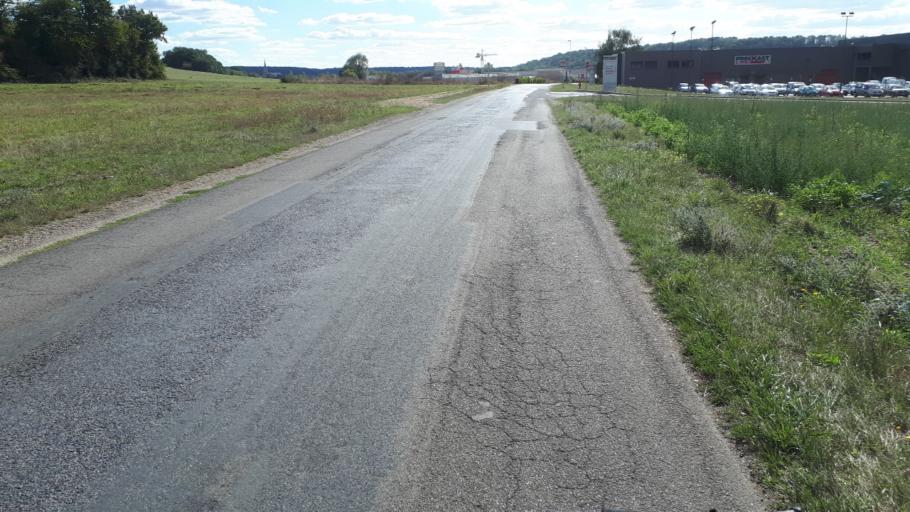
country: FR
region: Centre
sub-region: Departement du Loir-et-Cher
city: Villiers-sur-Loir
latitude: 47.8005
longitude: 0.9667
